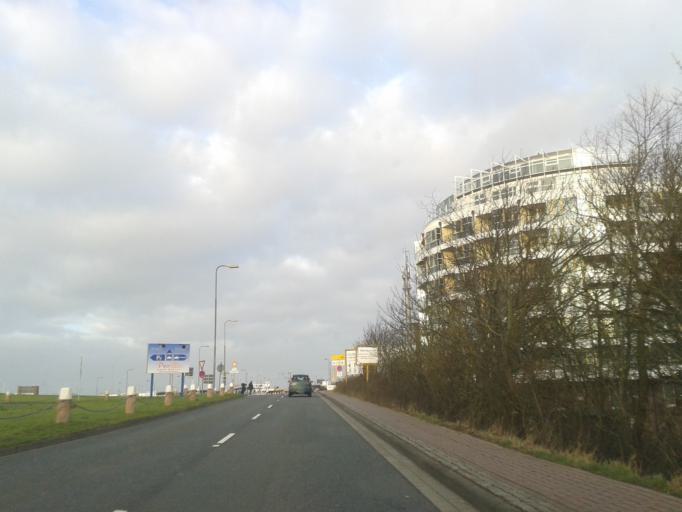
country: DE
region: Lower Saxony
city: Norddeich
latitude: 53.6210
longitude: 7.1579
